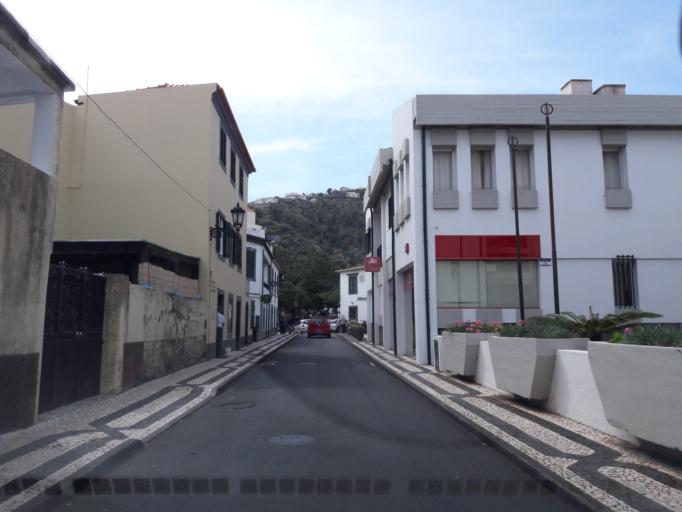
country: PT
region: Madeira
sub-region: Santa Cruz
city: Santa Cruz
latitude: 32.6883
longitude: -16.7913
